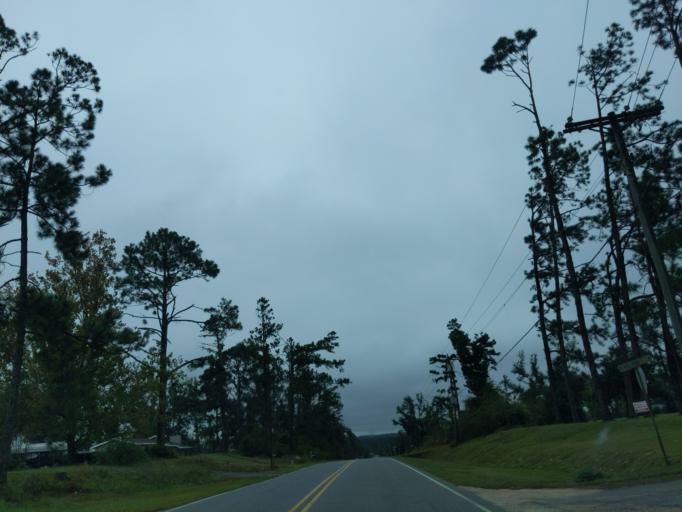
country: US
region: Florida
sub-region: Jackson County
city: Sneads
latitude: 30.7185
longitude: -84.9326
